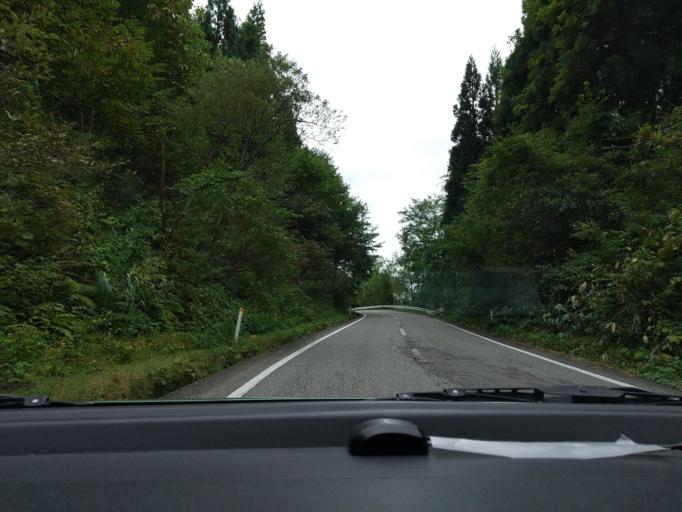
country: JP
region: Akita
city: Kakunodatemachi
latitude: 39.5506
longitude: 140.6343
